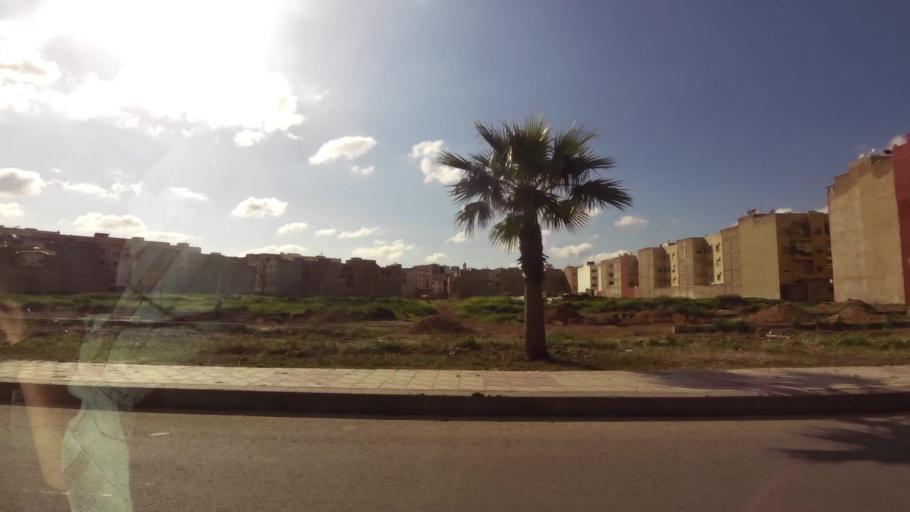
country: MA
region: Chaouia-Ouardigha
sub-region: Settat Province
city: Berrechid
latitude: 33.2732
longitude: -7.5843
